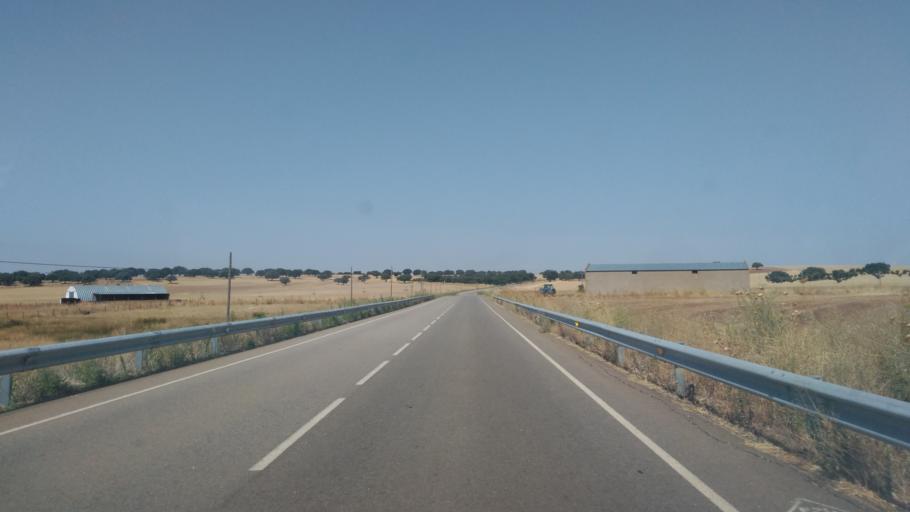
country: ES
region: Castille and Leon
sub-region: Provincia de Salamanca
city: Cabrillas
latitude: 40.7445
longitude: -6.1798
